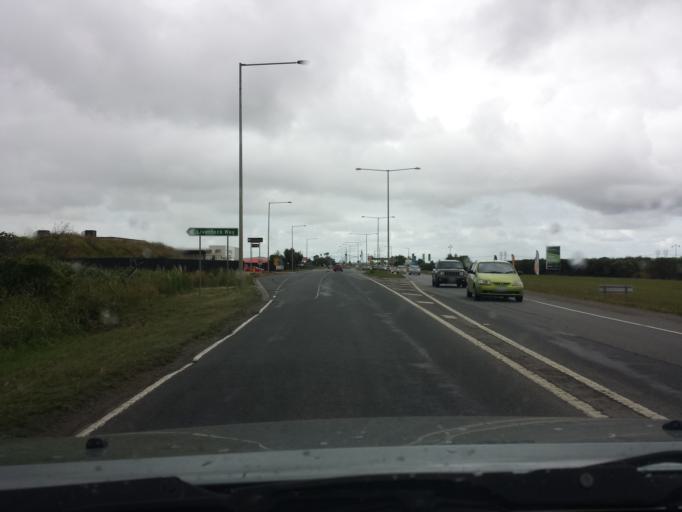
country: AU
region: Victoria
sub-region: Cardinia
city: Pakenham South
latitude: -38.0955
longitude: 145.4895
